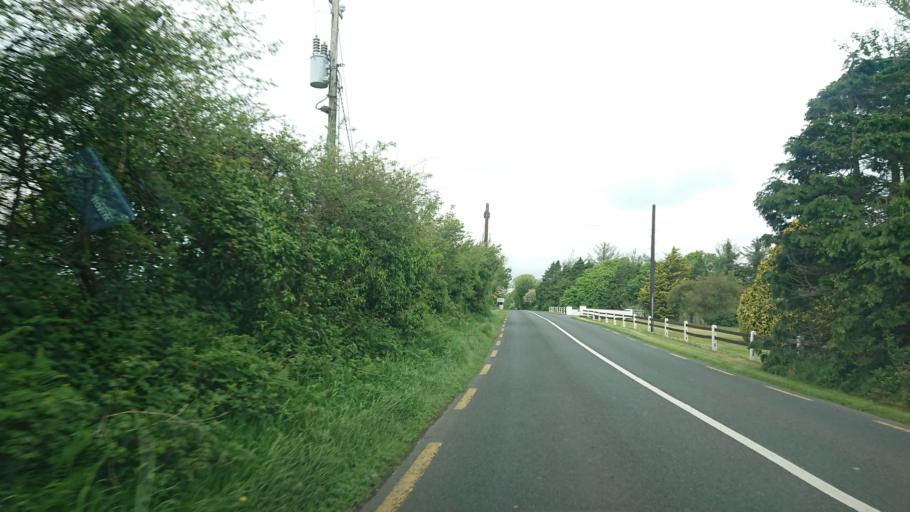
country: IE
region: Munster
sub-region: Waterford
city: Tra Mhor
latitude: 52.1811
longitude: -7.1706
